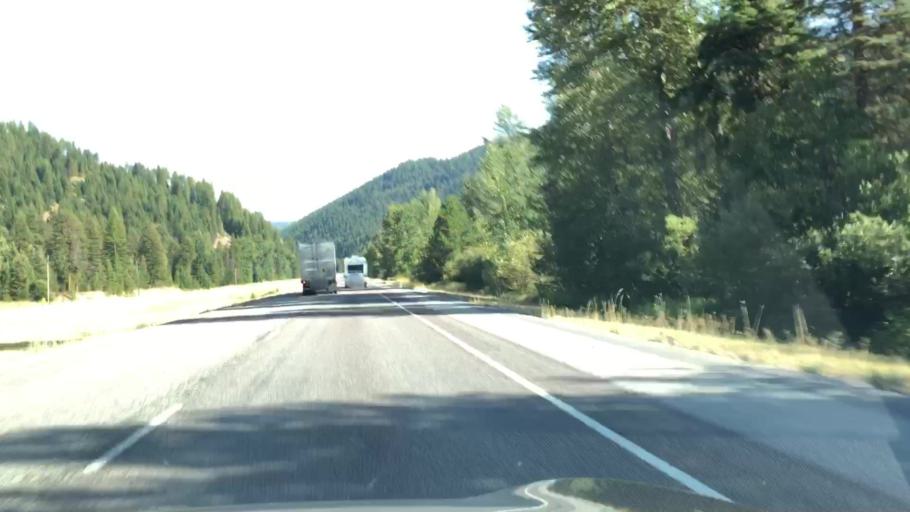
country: US
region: Montana
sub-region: Sanders County
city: Thompson Falls
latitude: 47.3651
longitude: -115.3282
